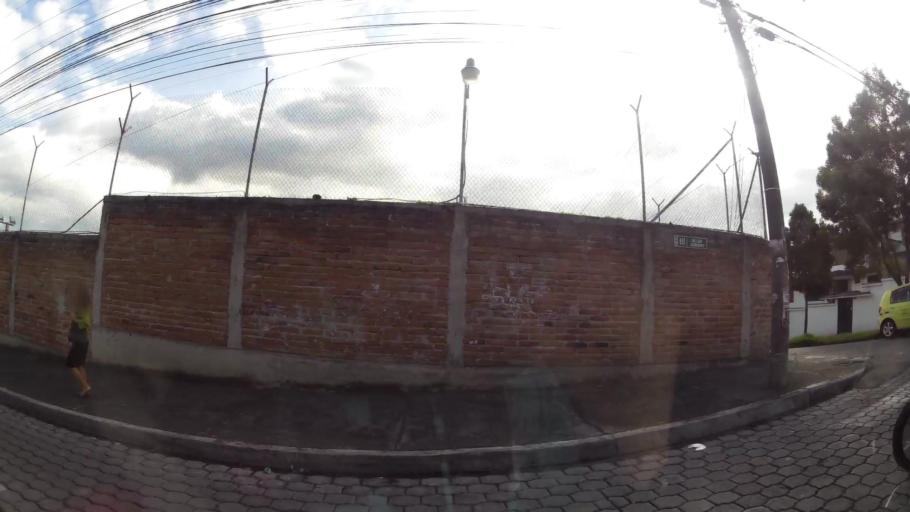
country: EC
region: Pichincha
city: Quito
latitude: -0.1342
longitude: -78.4717
